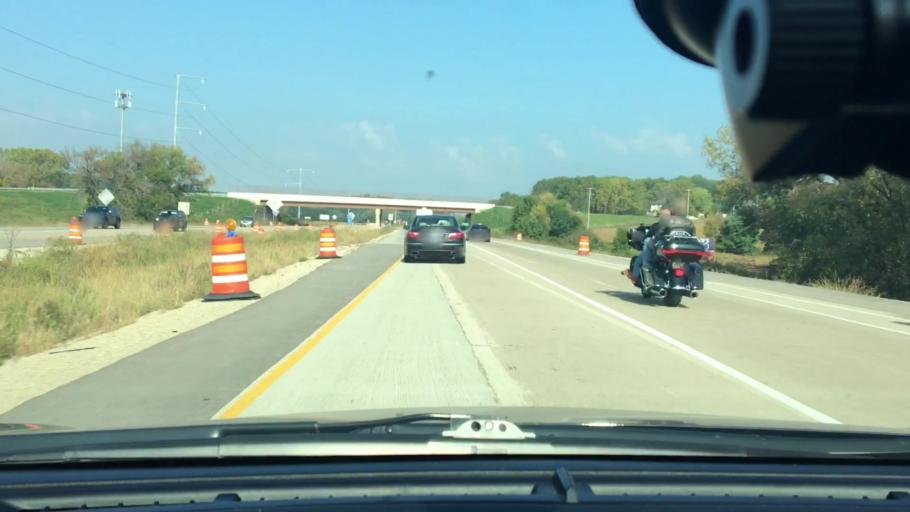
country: US
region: Wisconsin
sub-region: Dane County
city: McFarland
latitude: 43.0200
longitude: -89.2446
